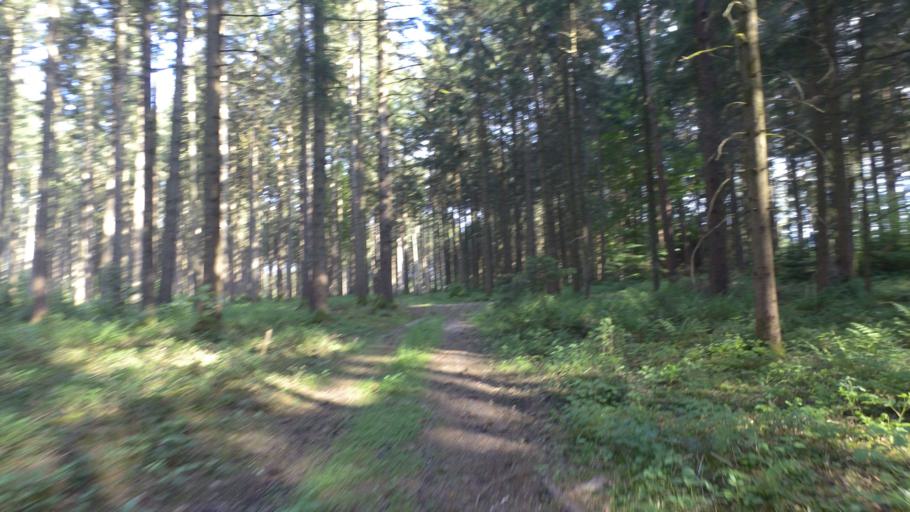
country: DE
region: Bavaria
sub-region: Upper Bavaria
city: Nussdorf
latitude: 47.8930
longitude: 12.5714
